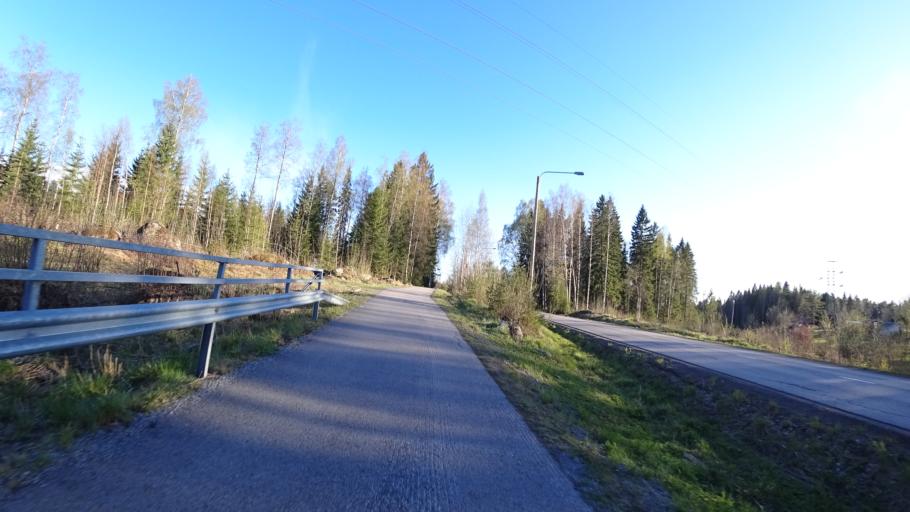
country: FI
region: Pirkanmaa
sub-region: Tampere
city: Yloejaervi
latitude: 61.5104
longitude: 23.5944
